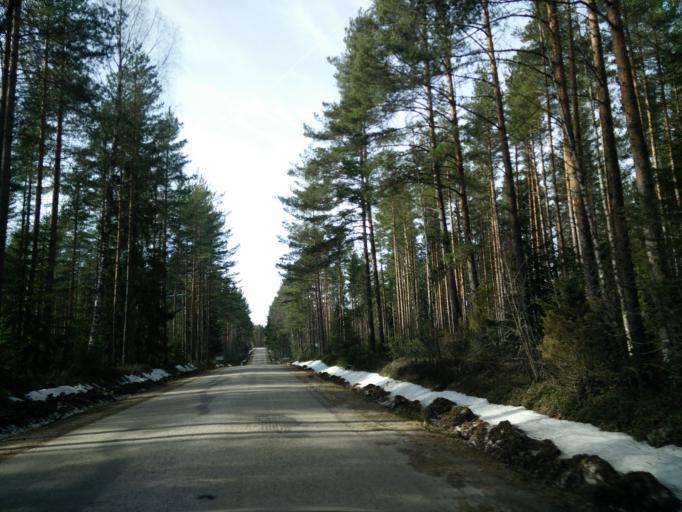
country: SE
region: Vaermland
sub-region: Hagfors Kommun
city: Hagfors
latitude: 60.0430
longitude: 13.5933
